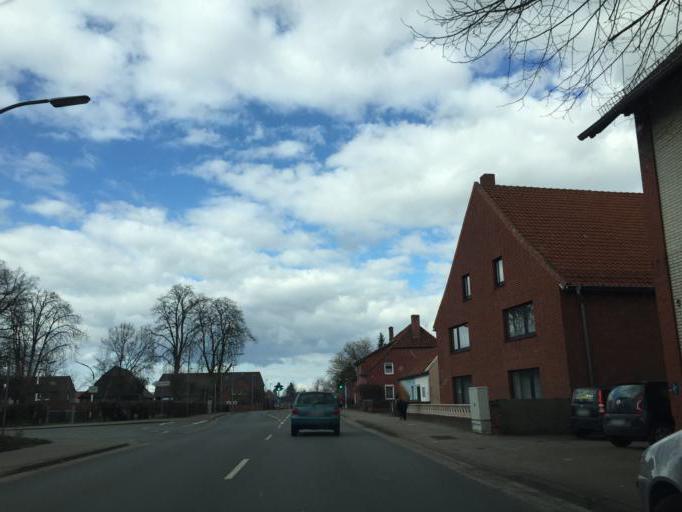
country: DE
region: Lower Saxony
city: Peine
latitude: 52.3479
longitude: 10.2420
